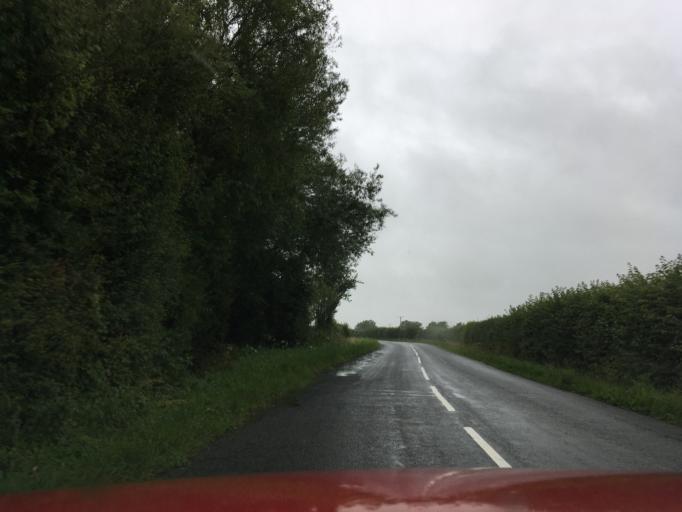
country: GB
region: England
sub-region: Gloucestershire
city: Uckington
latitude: 51.9242
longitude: -2.1369
